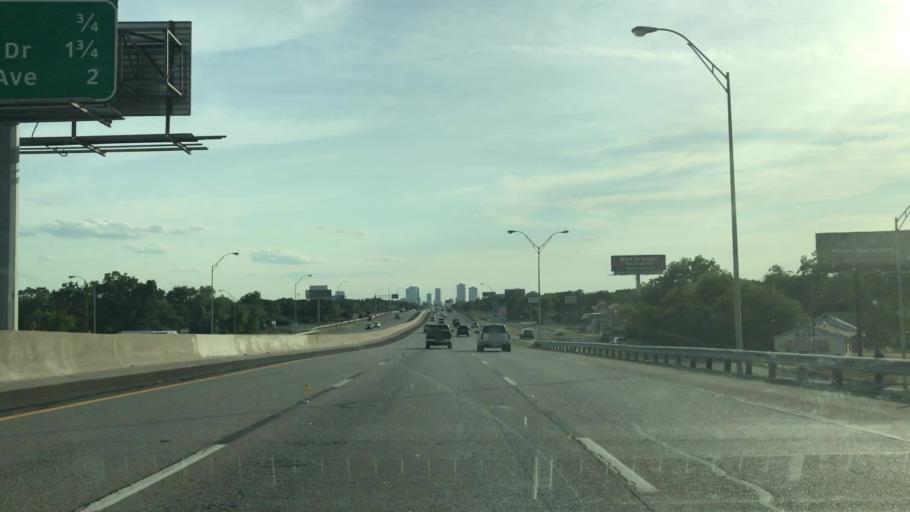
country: US
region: Texas
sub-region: Tarrant County
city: Haltom City
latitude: 32.7816
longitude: -97.2740
